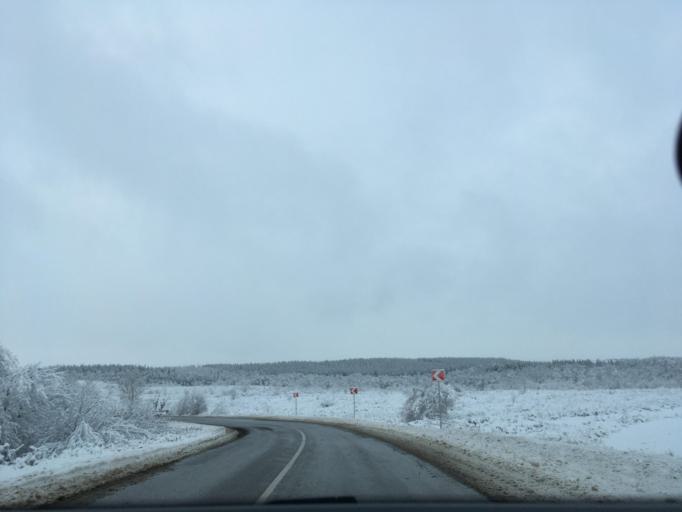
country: RU
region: Voronezj
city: Ol'khovatka
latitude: 50.1439
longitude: 39.2128
